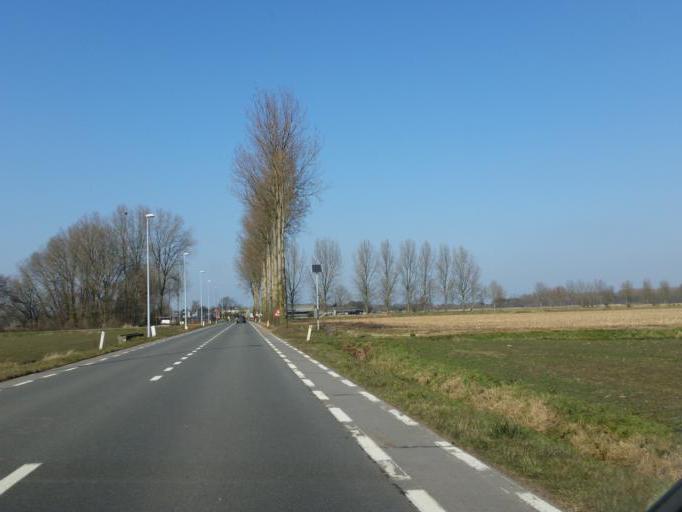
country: BE
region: Flanders
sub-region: Provincie Oost-Vlaanderen
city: Wachtebeke
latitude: 51.1561
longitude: 3.8629
